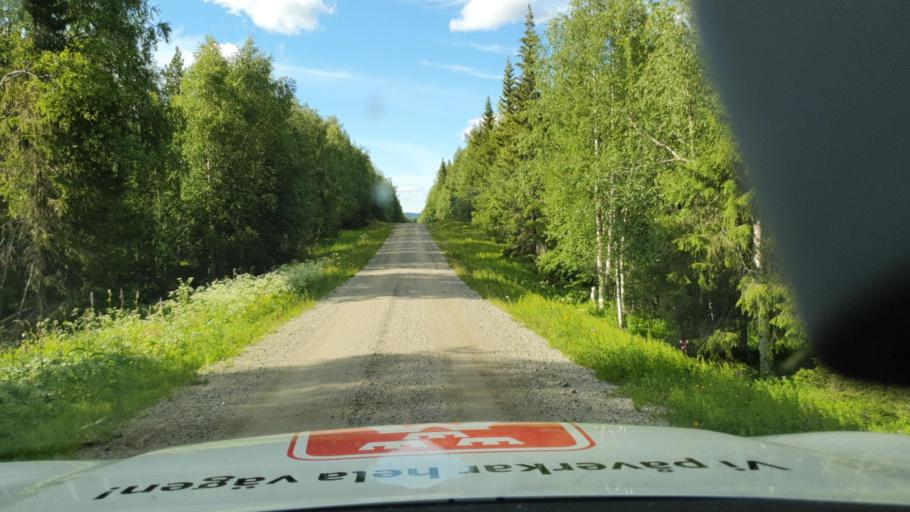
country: SE
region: Vaesterbotten
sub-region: Lycksele Kommun
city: Lycksele
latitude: 64.4296
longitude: 18.2751
